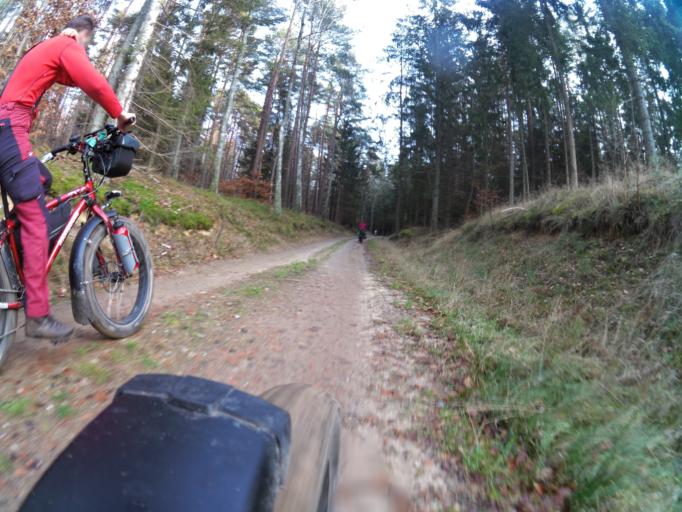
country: PL
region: West Pomeranian Voivodeship
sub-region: Powiat koszalinski
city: Polanow
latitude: 54.1433
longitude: 16.7040
